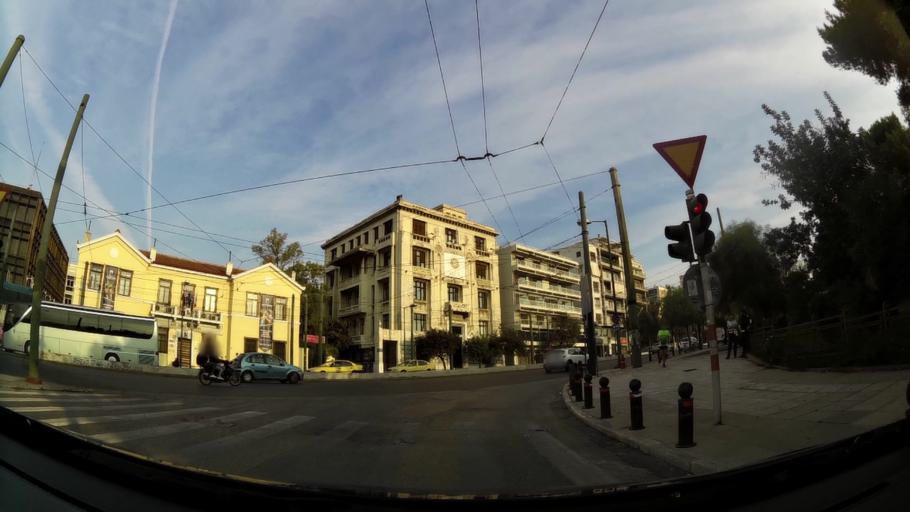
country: GR
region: Attica
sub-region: Nomarchia Athinas
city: Athens
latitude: 37.9710
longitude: 23.7333
